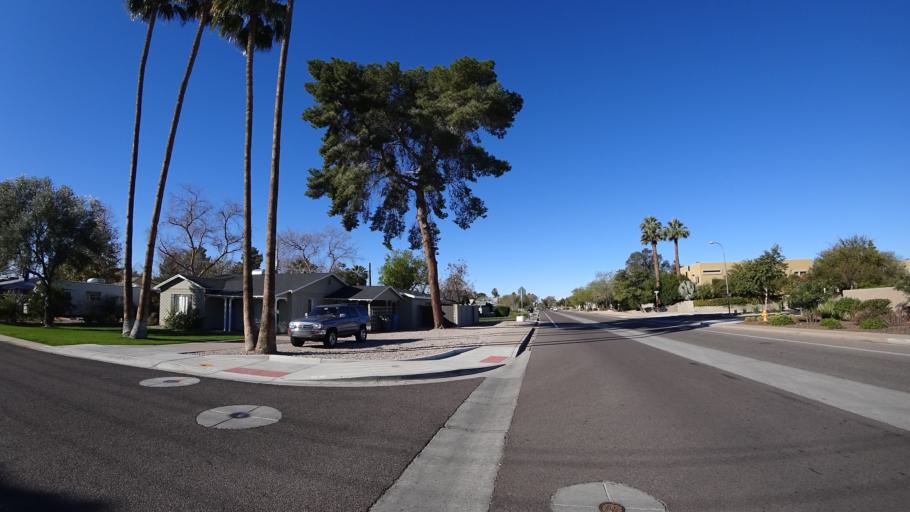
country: US
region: Arizona
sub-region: Maricopa County
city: Paradise Valley
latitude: 33.5025
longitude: -112.0096
